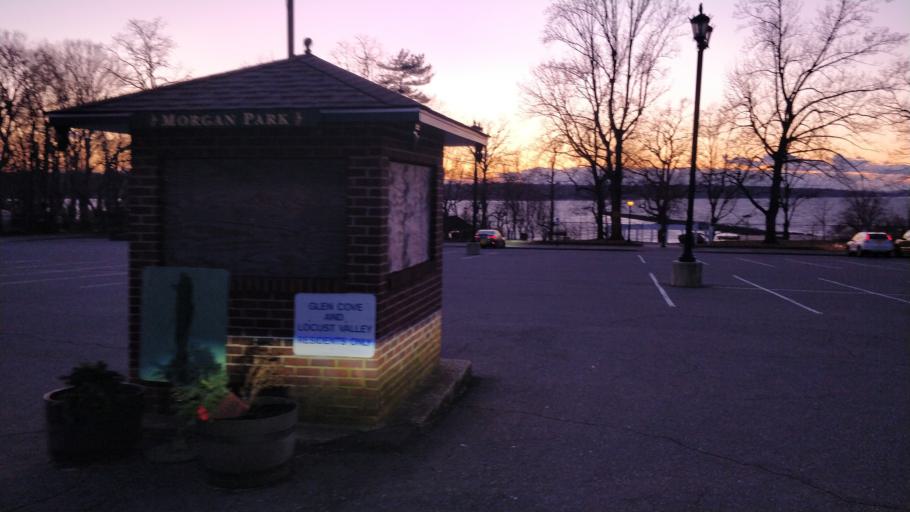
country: US
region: New York
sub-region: Nassau County
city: Sea Cliff
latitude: 40.8640
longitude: -73.6513
